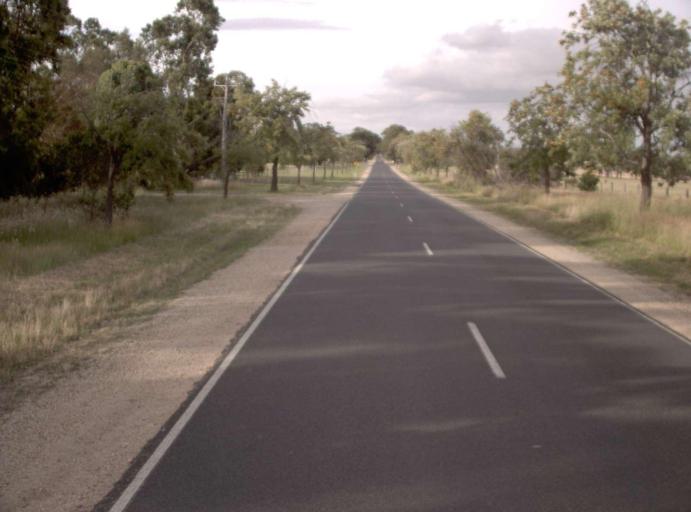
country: AU
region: Victoria
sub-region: Wellington
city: Sale
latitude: -37.9457
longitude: 146.9890
